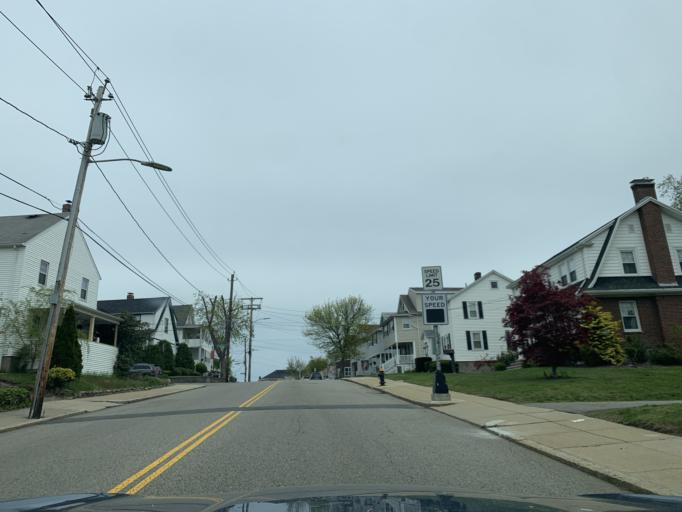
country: US
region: Massachusetts
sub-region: Norfolk County
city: Milton
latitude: 42.2794
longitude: -71.0510
